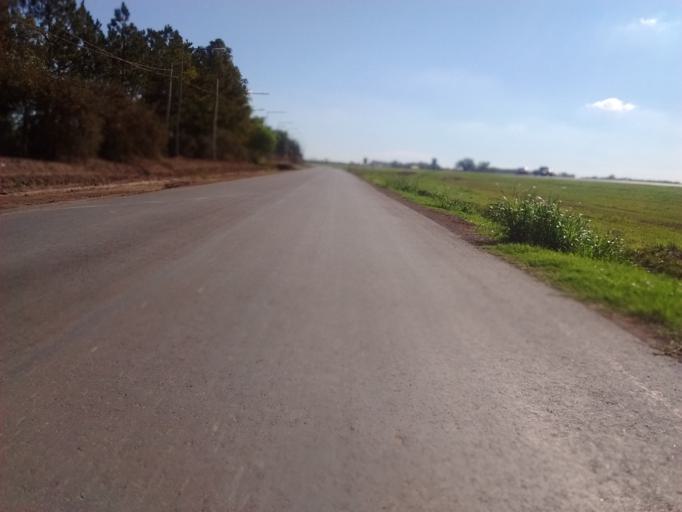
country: AR
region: Santa Fe
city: Roldan
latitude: -32.9292
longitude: -60.8824
